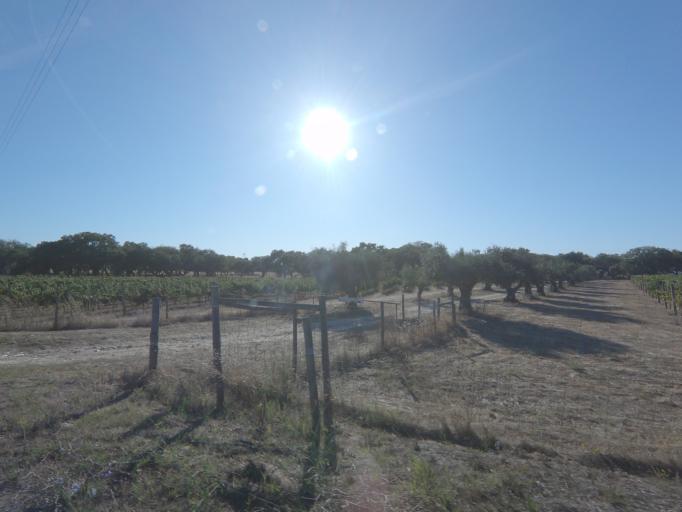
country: PT
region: Setubal
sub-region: Palmela
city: Quinta do Anjo
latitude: 38.5424
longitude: -8.9852
